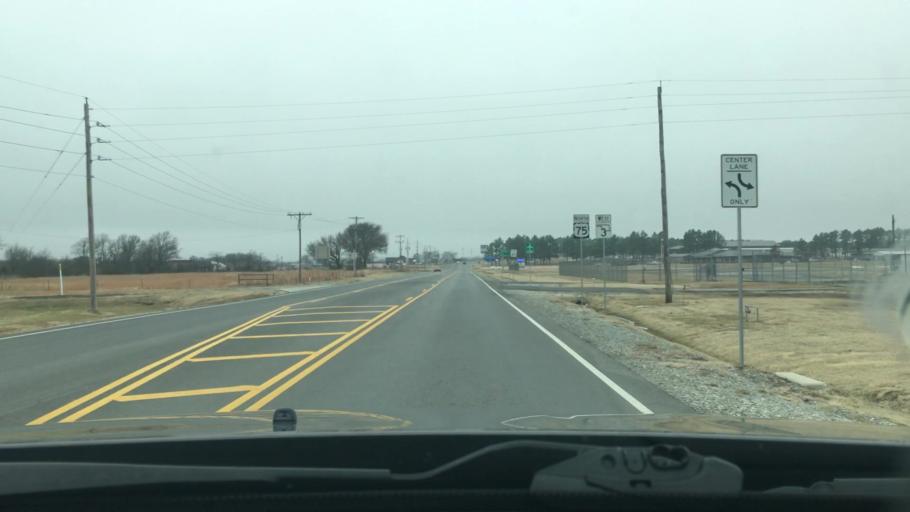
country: US
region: Oklahoma
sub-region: Atoka County
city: Atoka
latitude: 34.3942
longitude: -96.1462
